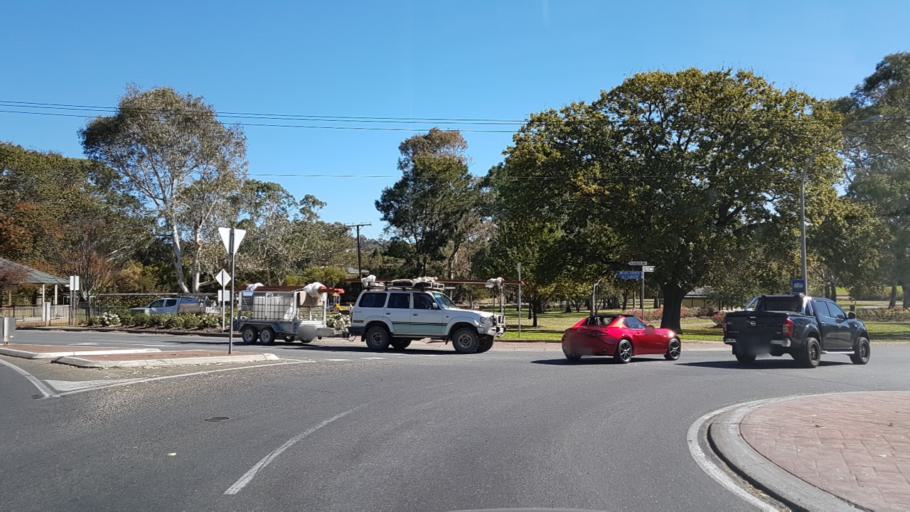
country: AU
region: South Australia
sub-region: Mount Barker
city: Mount Barker
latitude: -35.0733
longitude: 138.8575
